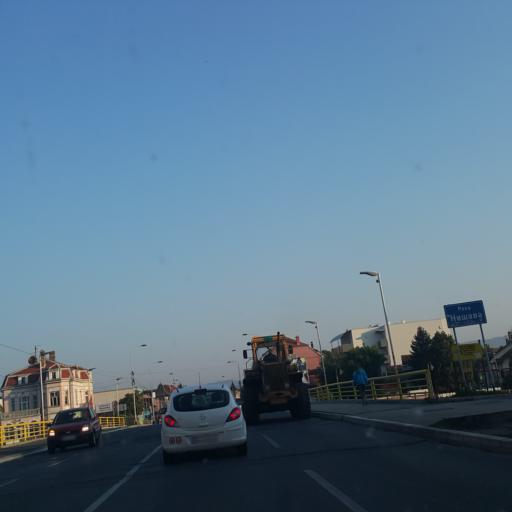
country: RS
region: Central Serbia
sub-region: Nisavski Okrug
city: Nis
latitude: 43.3209
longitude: 21.8908
